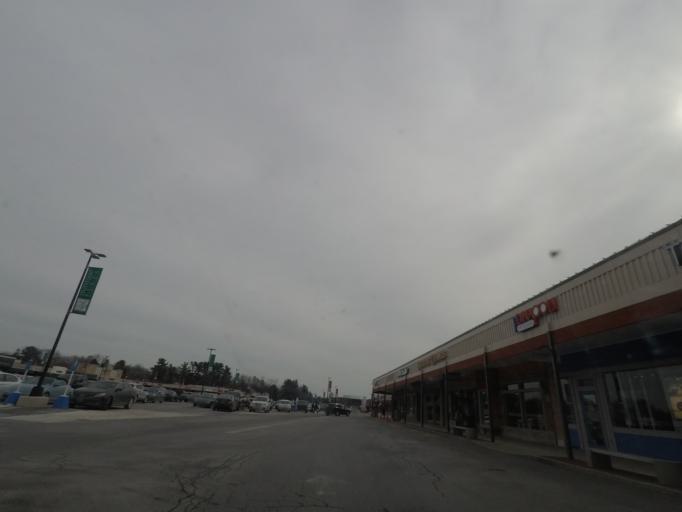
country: US
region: New York
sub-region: Albany County
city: McKownville
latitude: 42.6846
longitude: -73.8410
